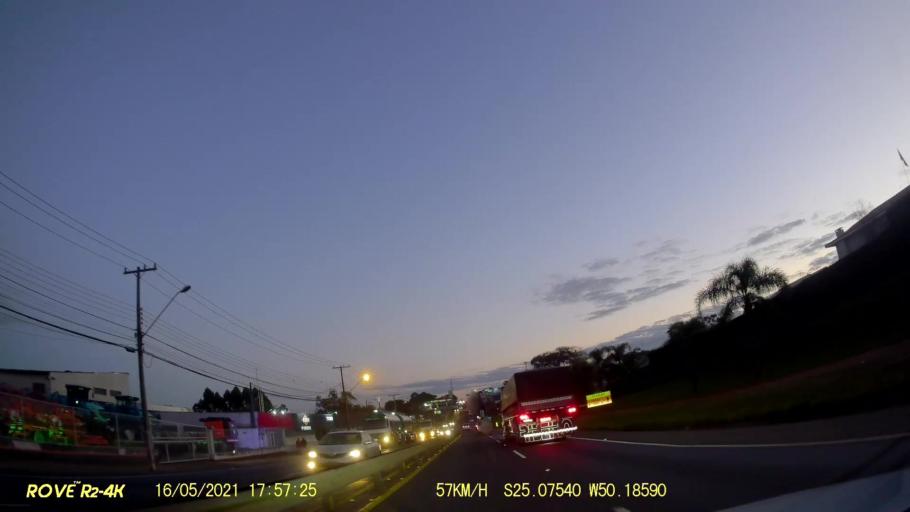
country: BR
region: Parana
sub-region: Ponta Grossa
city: Ponta Grossa
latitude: -25.0753
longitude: -50.1858
